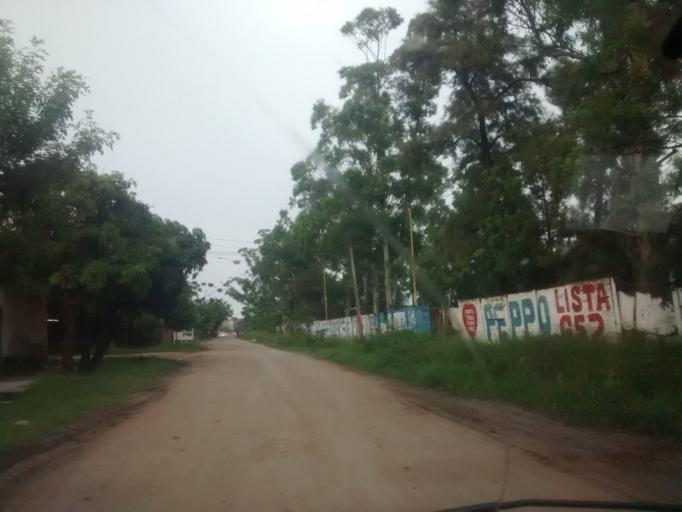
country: AR
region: Chaco
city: Resistencia
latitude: -27.4661
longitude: -58.9812
